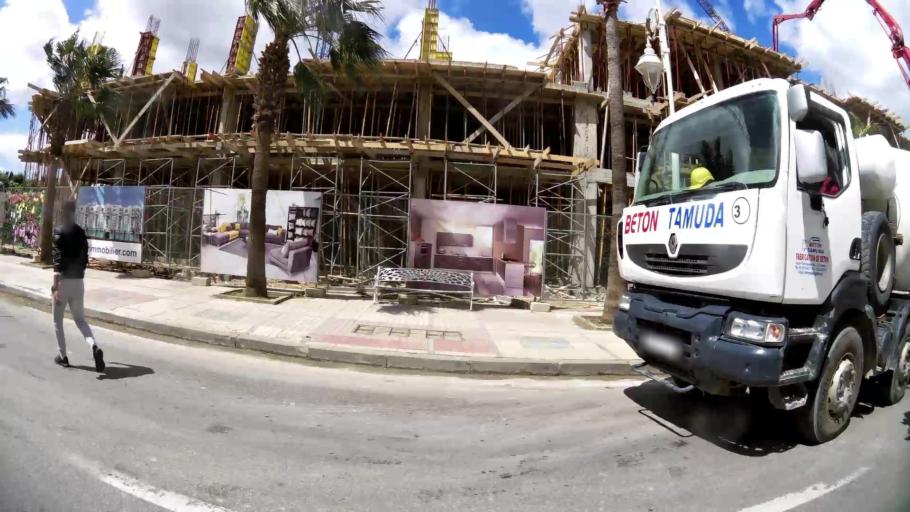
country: MA
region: Tanger-Tetouan
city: Tetouan
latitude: 35.5883
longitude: -5.3459
